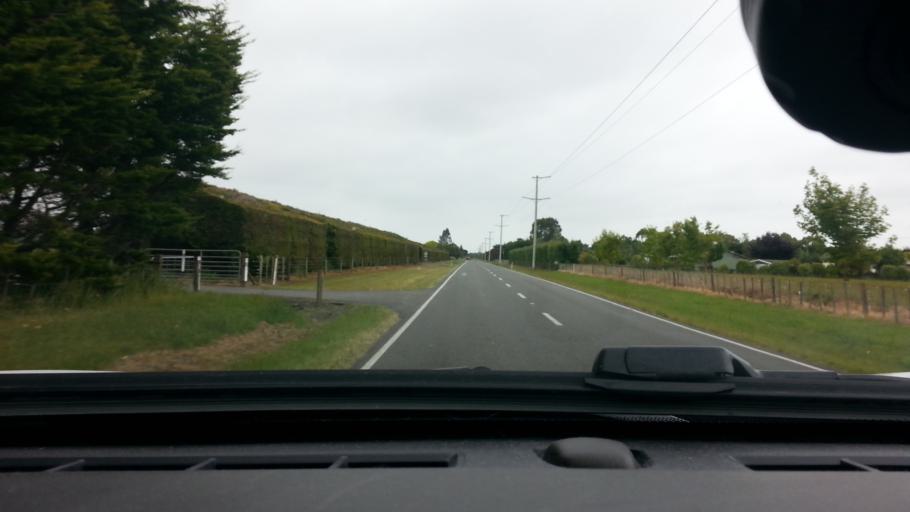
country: NZ
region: Wellington
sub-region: Masterton District
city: Masterton
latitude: -40.9121
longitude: 175.6413
